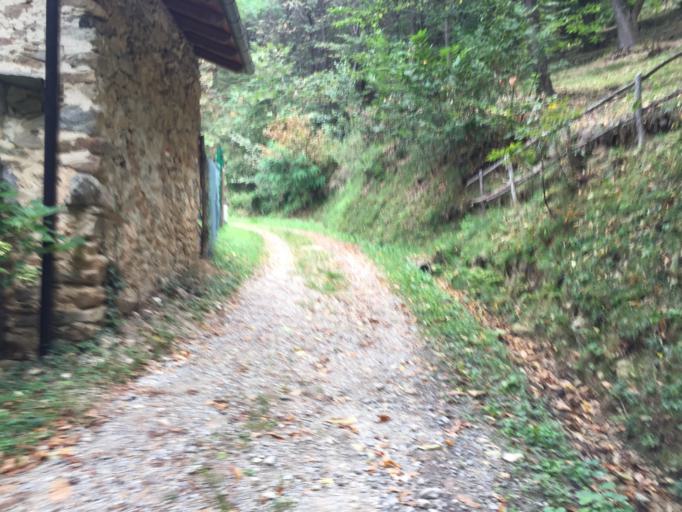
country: IT
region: Piedmont
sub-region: Provincia di Cuneo
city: Chiusa di Pesio
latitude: 44.3236
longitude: 7.6856
